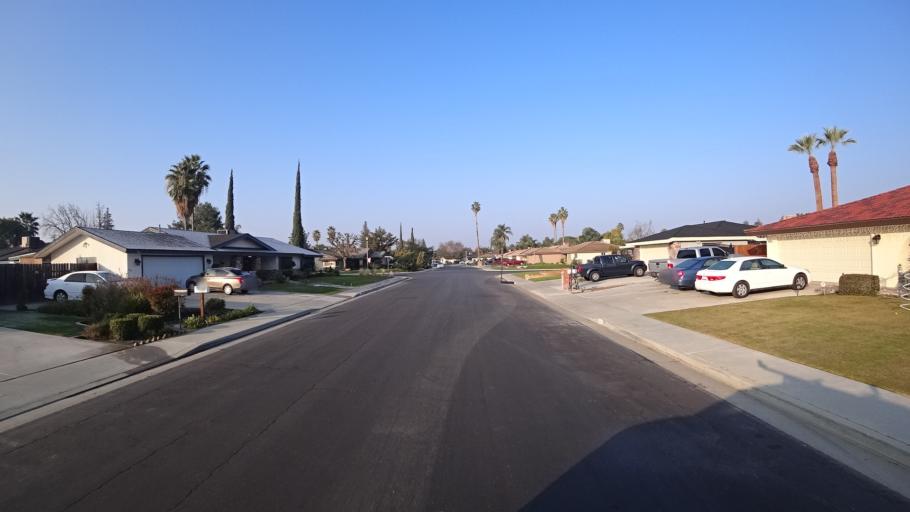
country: US
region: California
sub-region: Kern County
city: Greenacres
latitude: 35.3240
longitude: -119.0766
